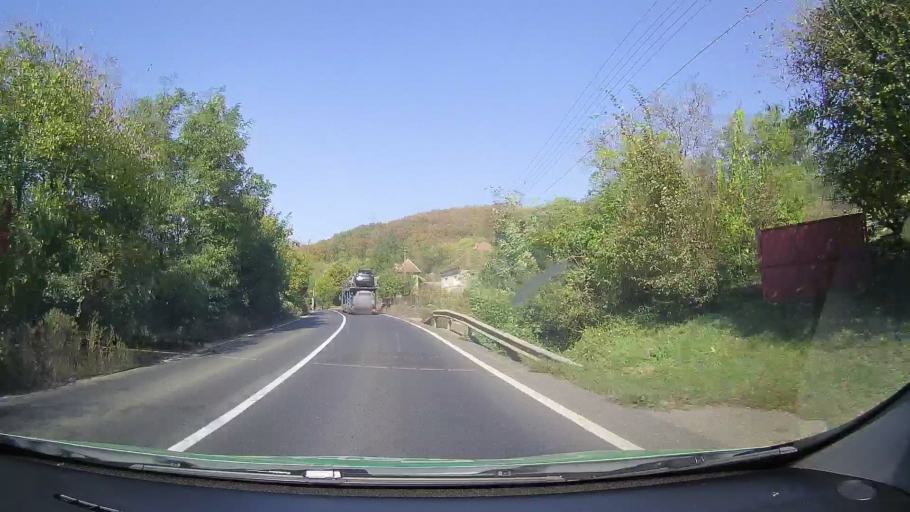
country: RO
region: Arad
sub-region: Comuna Bata
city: Bata
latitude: 46.0466
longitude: 22.0593
